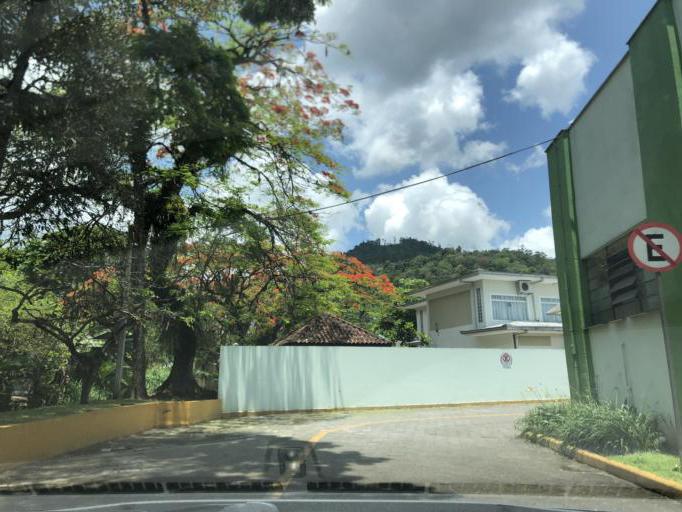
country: BR
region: Santa Catarina
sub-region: Jaragua Do Sul
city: Jaragua do Sul
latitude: -26.5051
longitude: -49.0902
